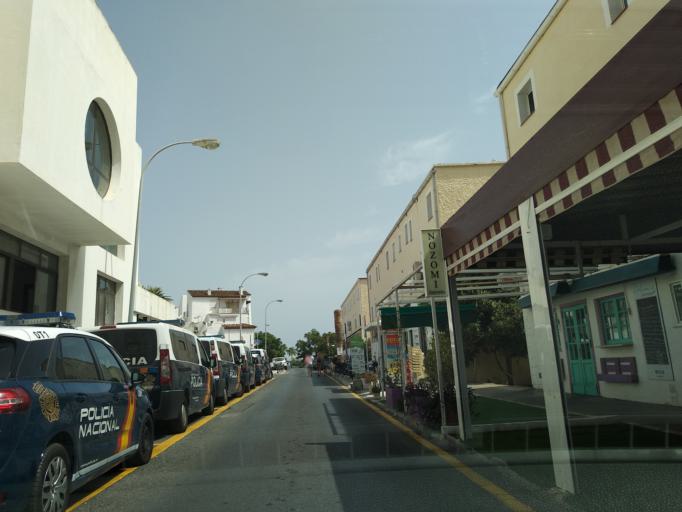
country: ES
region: Andalusia
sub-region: Provincia de Malaga
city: Torremolinos
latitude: 36.6195
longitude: -4.4985
